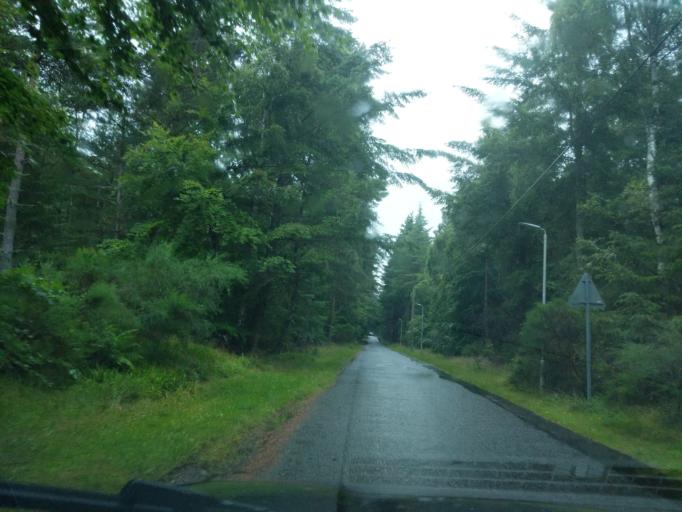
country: GB
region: Scotland
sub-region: Aberdeenshire
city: Aboyne
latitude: 57.0699
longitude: -2.8016
